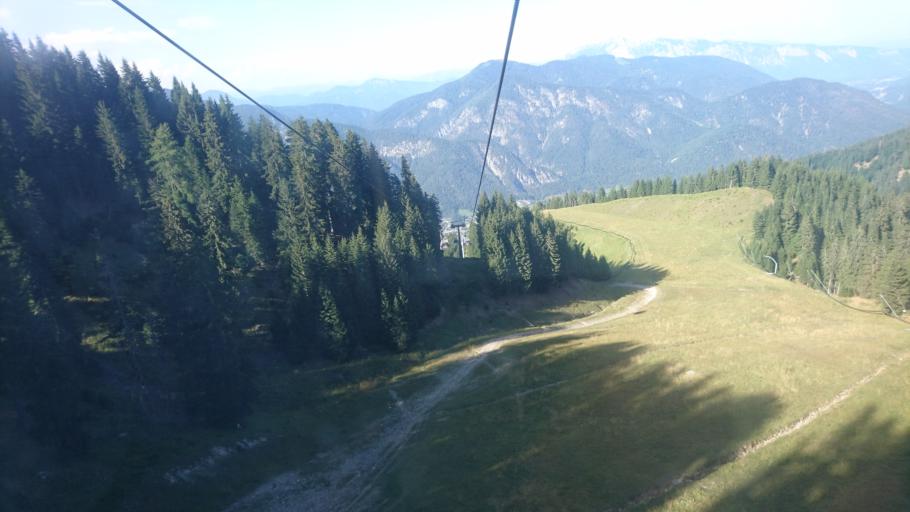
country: IT
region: Friuli Venezia Giulia
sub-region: Provincia di Udine
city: Tarvisio
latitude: 46.4846
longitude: 13.5227
